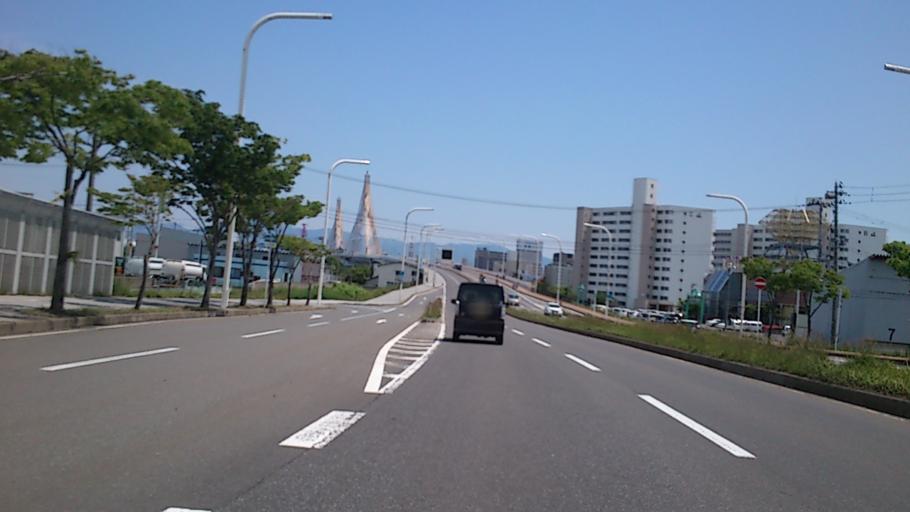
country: JP
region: Aomori
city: Aomori Shi
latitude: 40.8336
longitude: 140.7283
